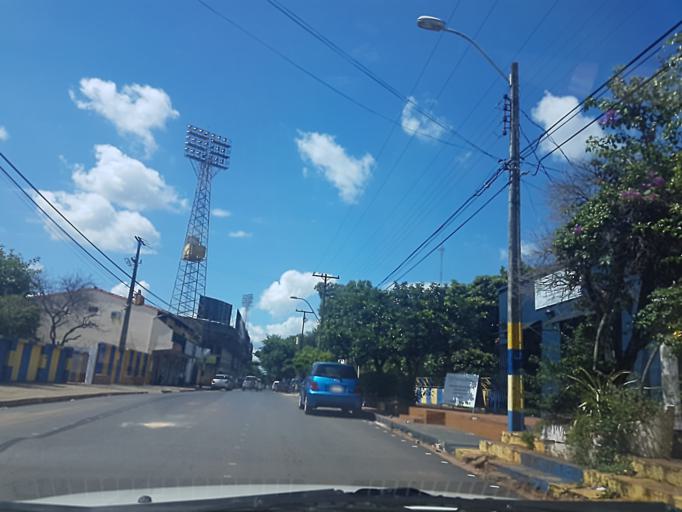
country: PY
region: Central
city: San Lorenzo
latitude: -25.2739
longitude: -57.4928
